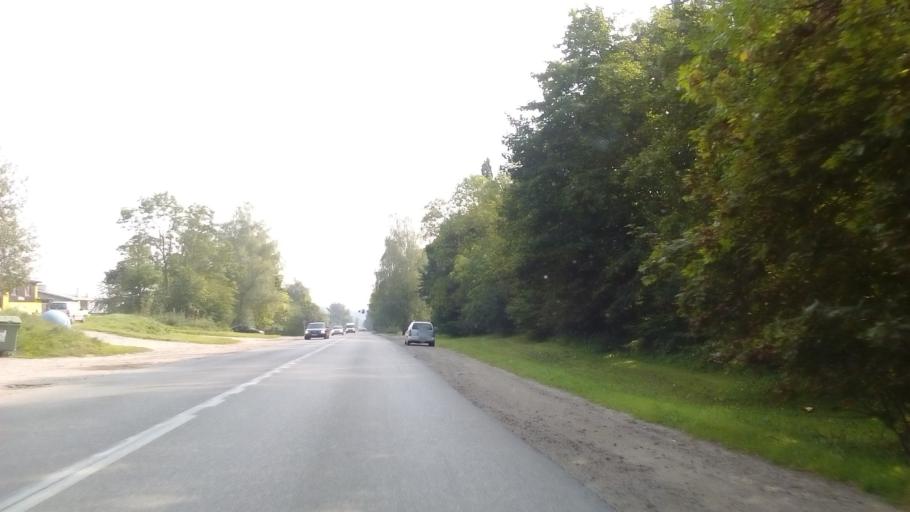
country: LT
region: Alytaus apskritis
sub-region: Alytus
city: Alytus
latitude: 54.3868
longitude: 24.0207
